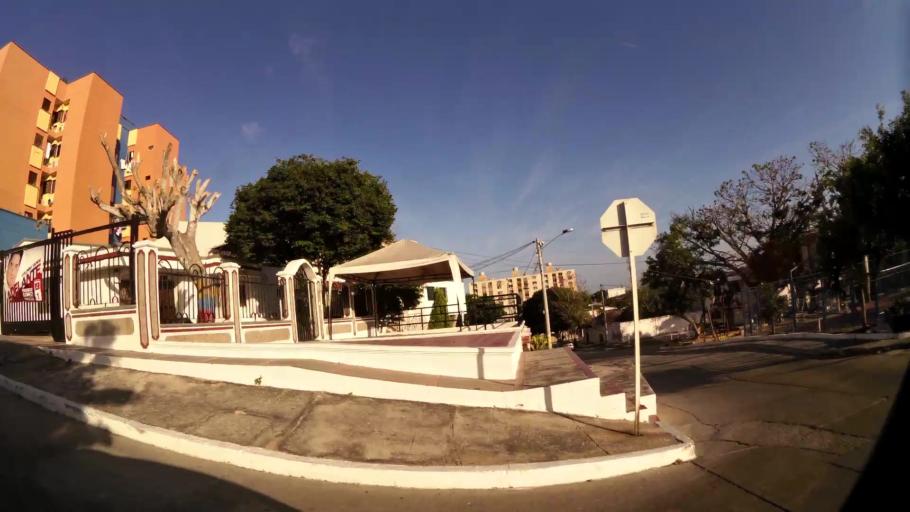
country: CO
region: Atlantico
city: Barranquilla
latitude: 10.9822
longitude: -74.8054
